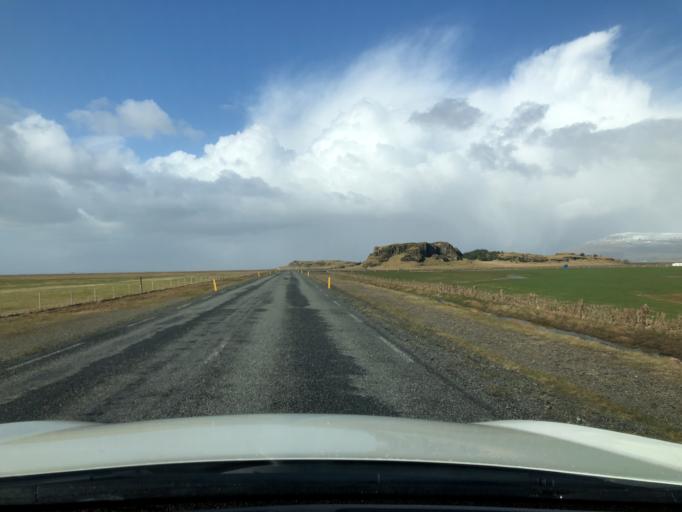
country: IS
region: East
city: Hoefn
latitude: 64.2713
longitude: -15.4948
